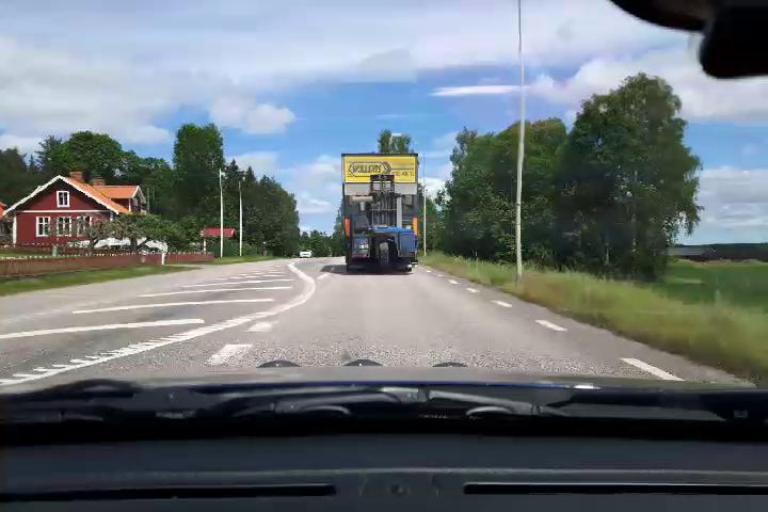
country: SE
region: Uppsala
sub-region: Osthammars Kommun
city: Bjorklinge
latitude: 60.0859
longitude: 17.5503
